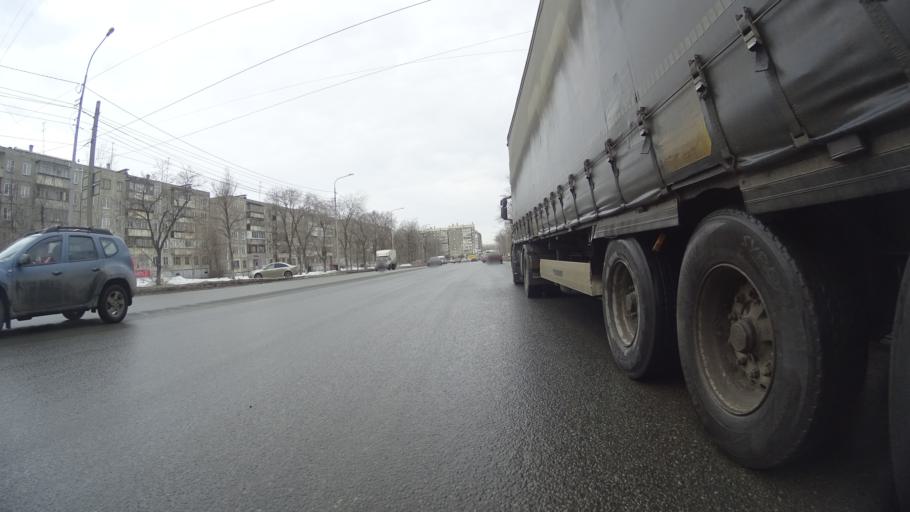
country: RU
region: Chelyabinsk
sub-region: Gorod Chelyabinsk
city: Chelyabinsk
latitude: 55.1957
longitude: 61.3327
